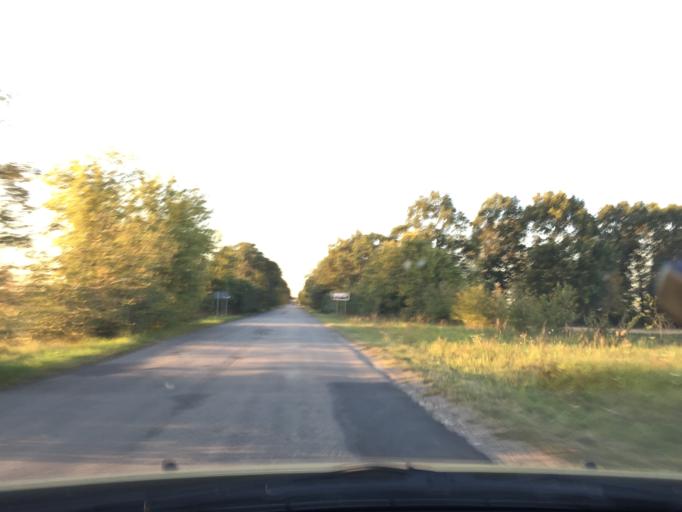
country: PL
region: Greater Poland Voivodeship
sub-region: Powiat pleszewski
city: Dobrzyca
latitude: 51.8423
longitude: 17.6201
